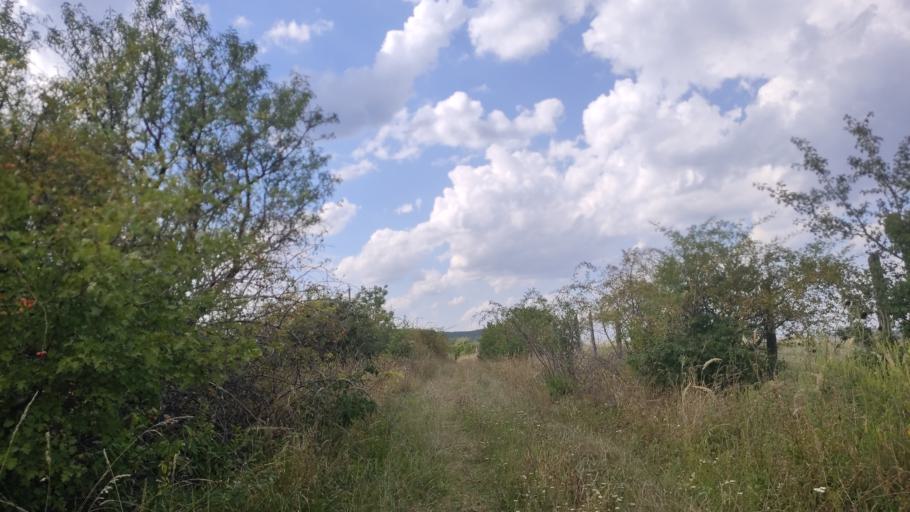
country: HU
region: Pest
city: Toeroekbalint
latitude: 47.4513
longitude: 18.8732
